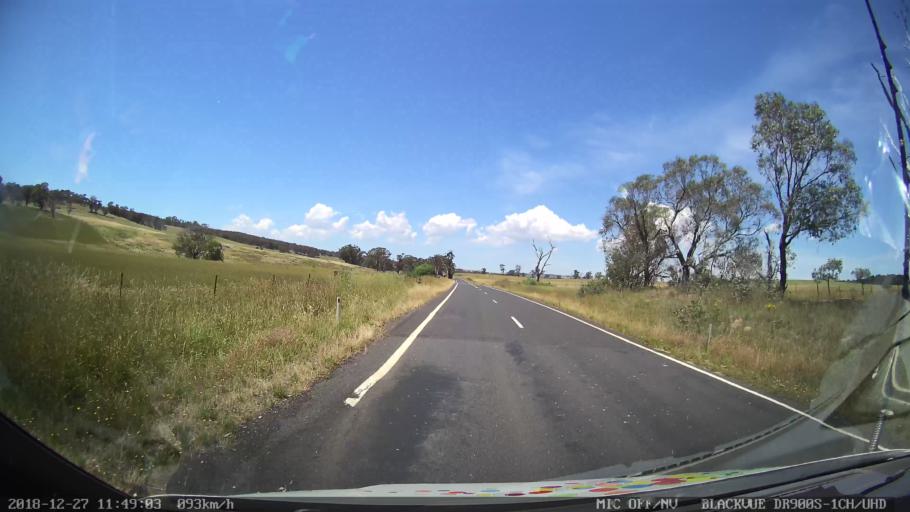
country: AU
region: New South Wales
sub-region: Bathurst Regional
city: Perthville
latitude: -33.6135
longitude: 149.4352
